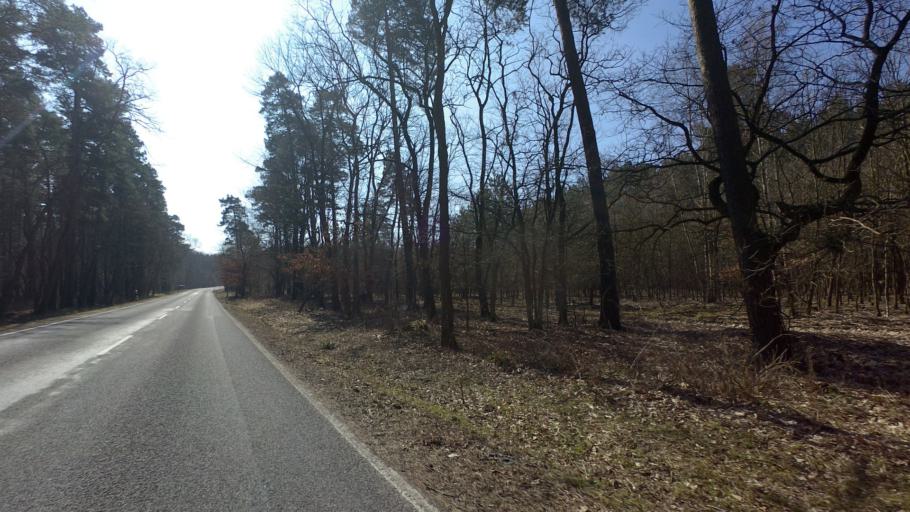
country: DE
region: Saxony-Anhalt
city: Nudersdorf
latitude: 51.9724
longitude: 12.5872
